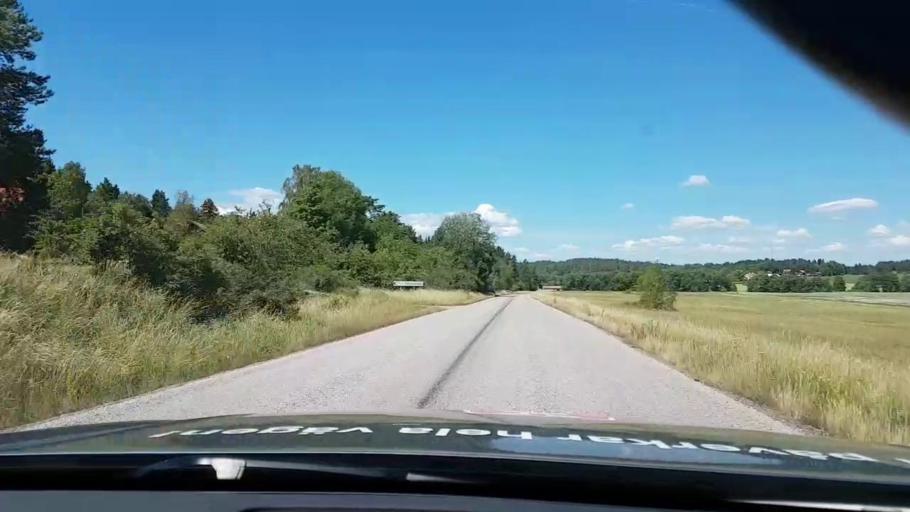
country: SE
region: Kalmar
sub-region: Vasterviks Kommun
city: Forserum
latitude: 57.9437
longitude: 16.4507
